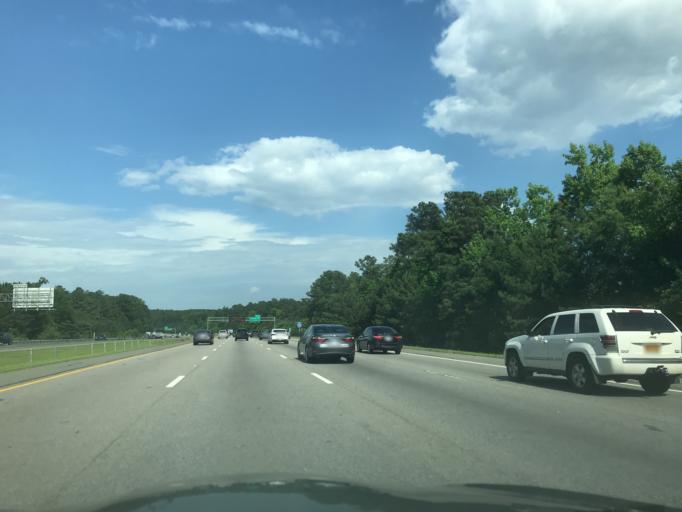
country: US
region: North Carolina
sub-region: Wake County
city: Morrisville
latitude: 35.8945
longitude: -78.7996
